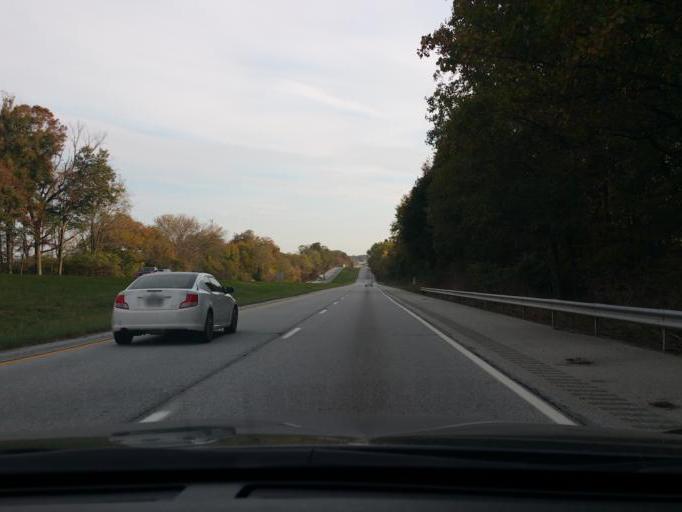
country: US
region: Pennsylvania
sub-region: Chester County
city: Oxford
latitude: 39.7648
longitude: -76.0156
